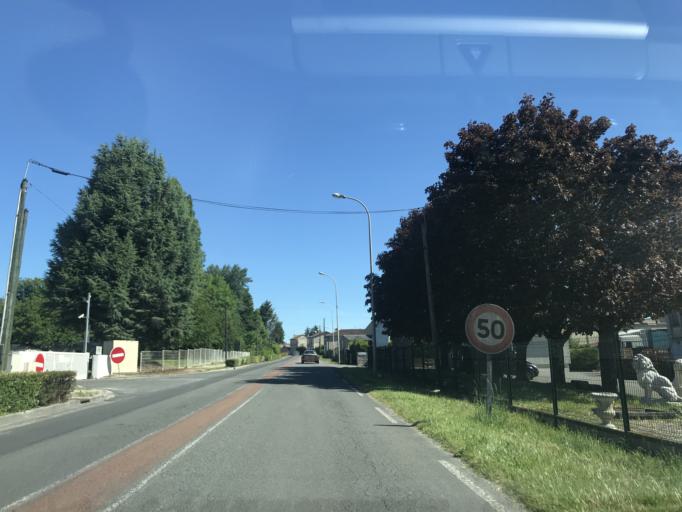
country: FR
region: Poitou-Charentes
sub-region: Departement de la Charente
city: Barbezieux-Saint-Hilaire
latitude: 45.4669
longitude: -0.1514
